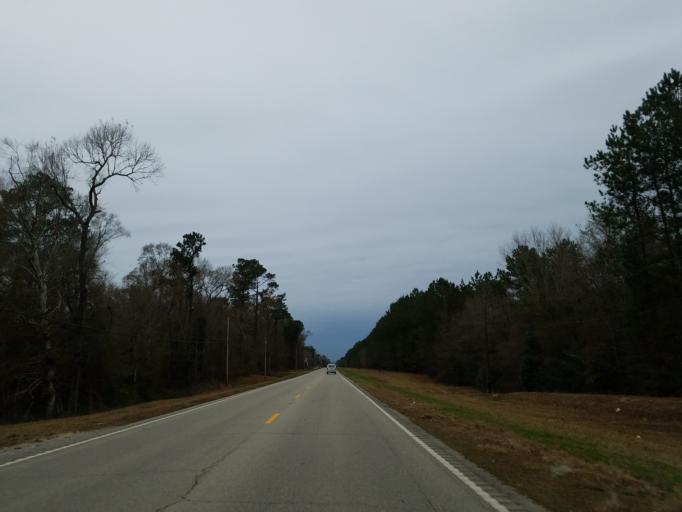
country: US
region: Mississippi
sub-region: Forrest County
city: Glendale
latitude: 31.4233
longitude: -89.2806
